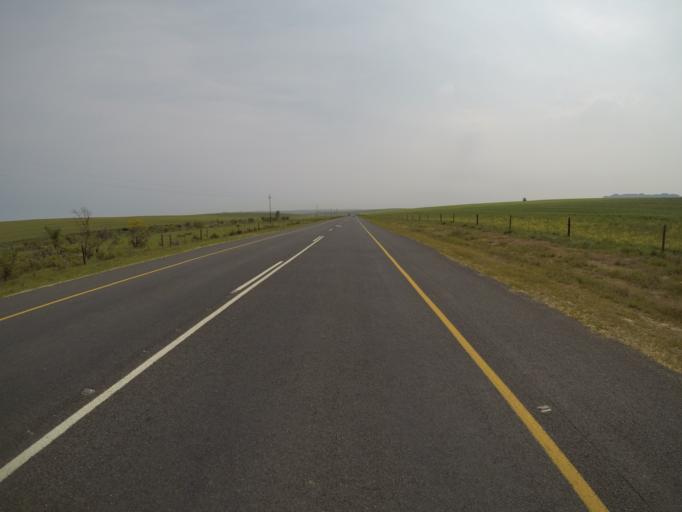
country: ZA
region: Western Cape
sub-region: West Coast District Municipality
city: Malmesbury
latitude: -33.4713
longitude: 18.7941
